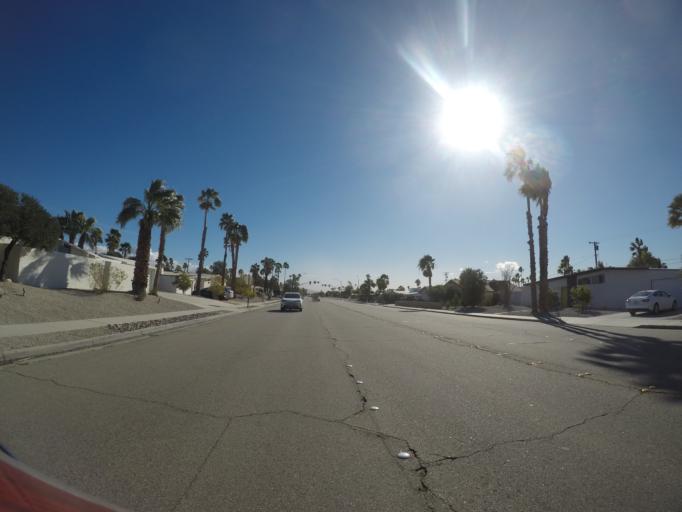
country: US
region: California
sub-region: Riverside County
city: Palm Springs
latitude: 33.8522
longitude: -116.5383
